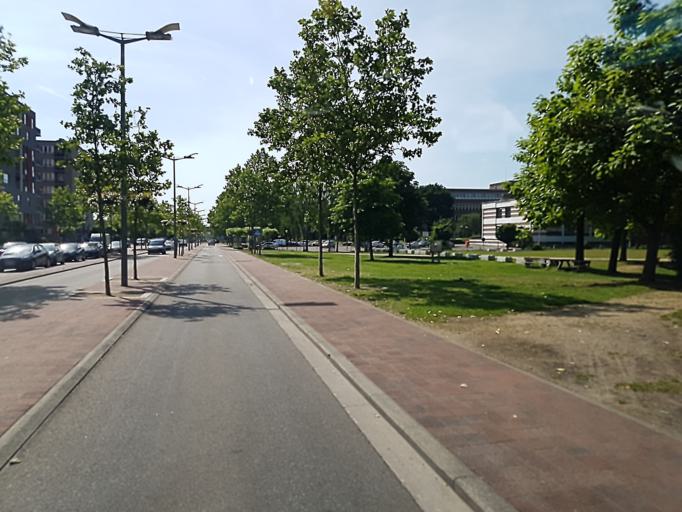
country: BE
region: Flanders
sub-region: Provincie Limburg
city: Genk
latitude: 50.9645
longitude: 5.4927
